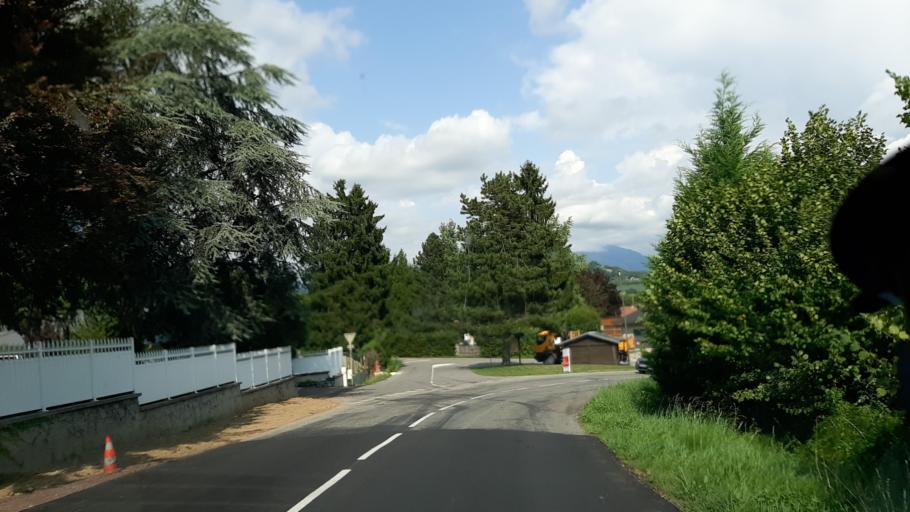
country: FR
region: Rhone-Alpes
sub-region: Departement de la Savoie
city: Mercury
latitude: 45.6686
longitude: 6.3395
